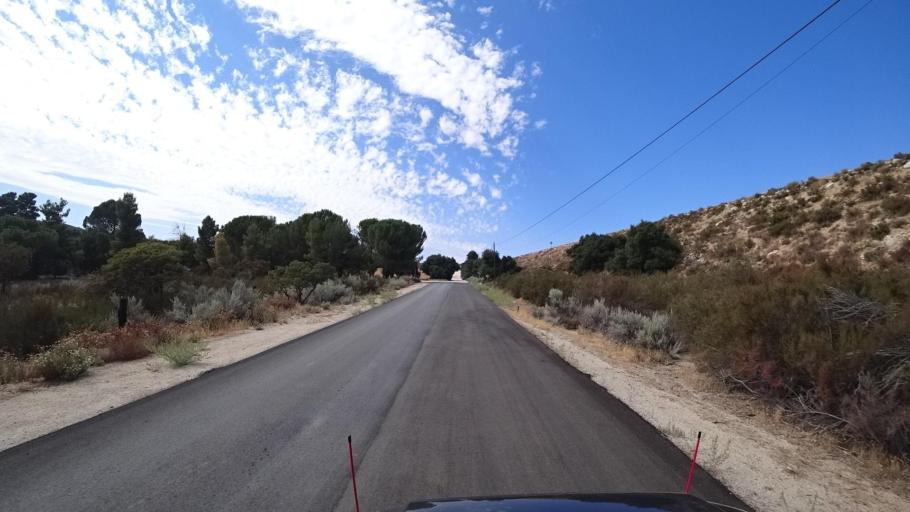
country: US
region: California
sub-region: San Diego County
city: Campo
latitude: 32.6798
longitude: -116.2965
